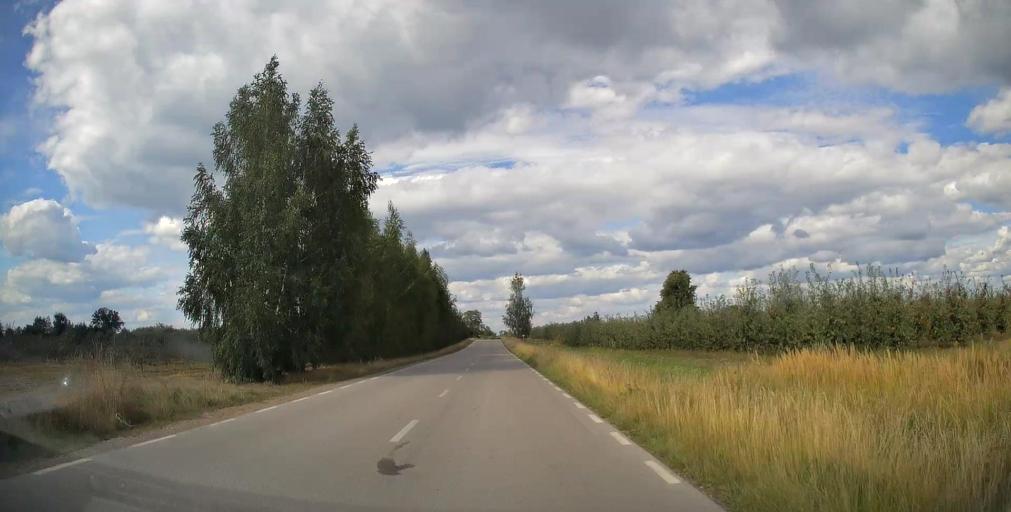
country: PL
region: Masovian Voivodeship
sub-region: Powiat grojecki
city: Goszczyn
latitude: 51.7535
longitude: 20.9032
